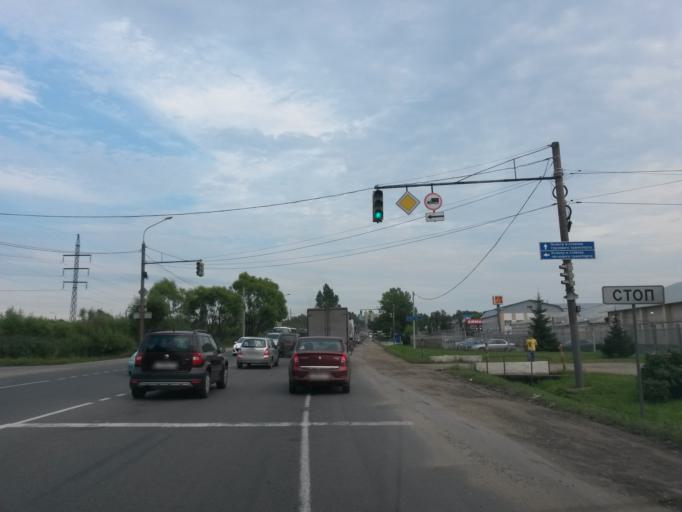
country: RU
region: Jaroslavl
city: Yaroslavl
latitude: 57.5955
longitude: 39.8112
